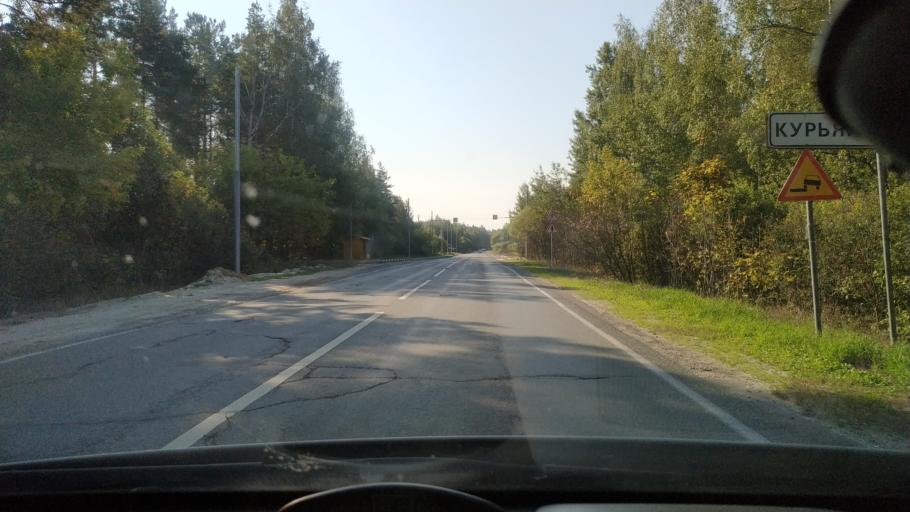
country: RU
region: Moskovskaya
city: Tugolesskiy Bor
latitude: 55.5359
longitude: 39.7072
